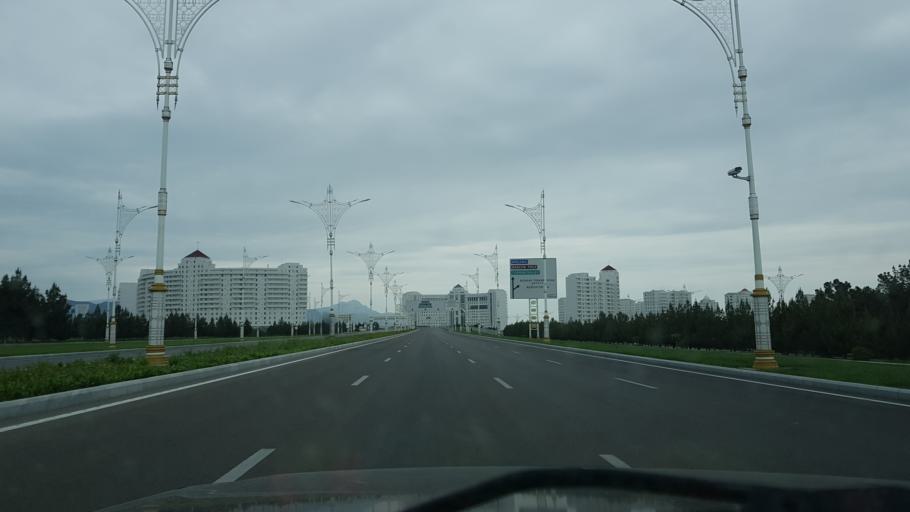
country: TM
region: Ahal
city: Ashgabat
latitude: 37.8918
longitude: 58.3442
